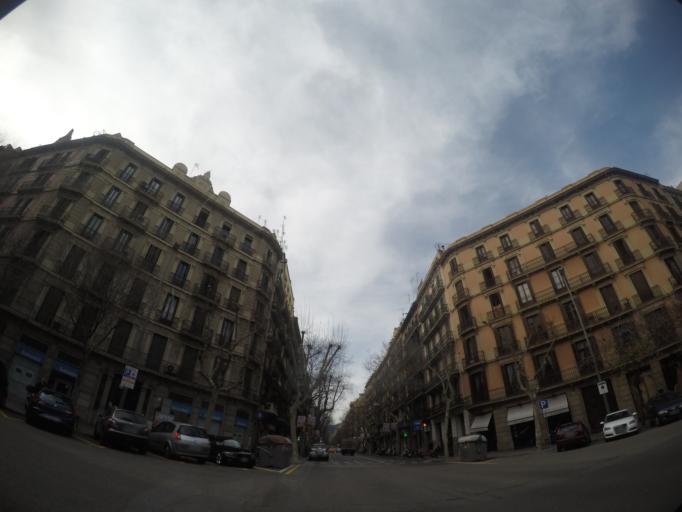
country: ES
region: Catalonia
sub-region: Provincia de Barcelona
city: Barcelona
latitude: 41.3884
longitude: 2.1598
